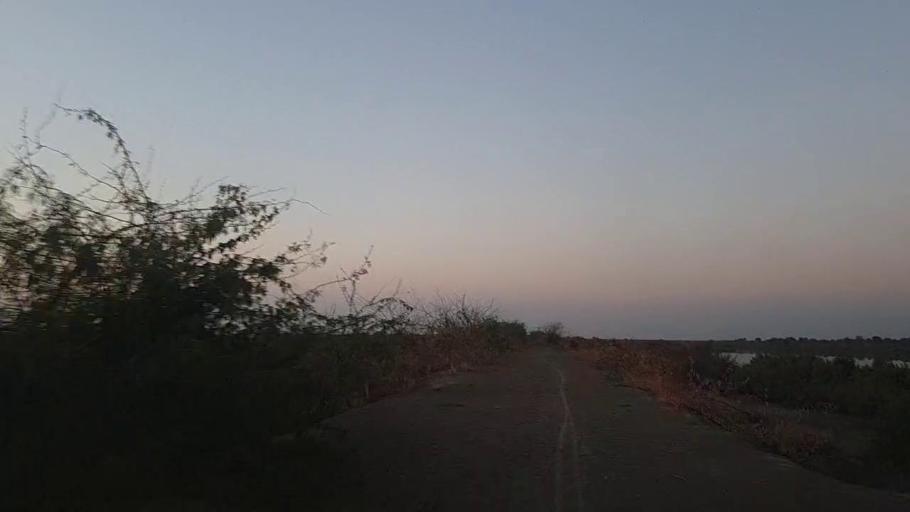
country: PK
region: Sindh
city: Tando Mittha Khan
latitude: 26.0793
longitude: 69.1525
